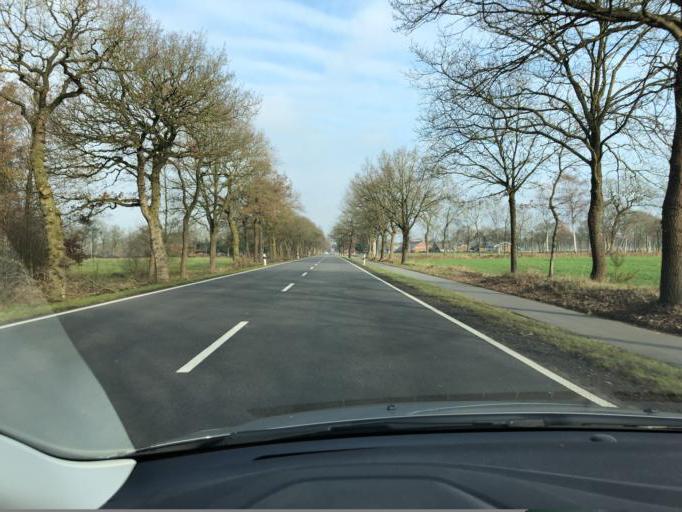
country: DE
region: Lower Saxony
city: Hesel
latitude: 53.3263
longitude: 7.6015
